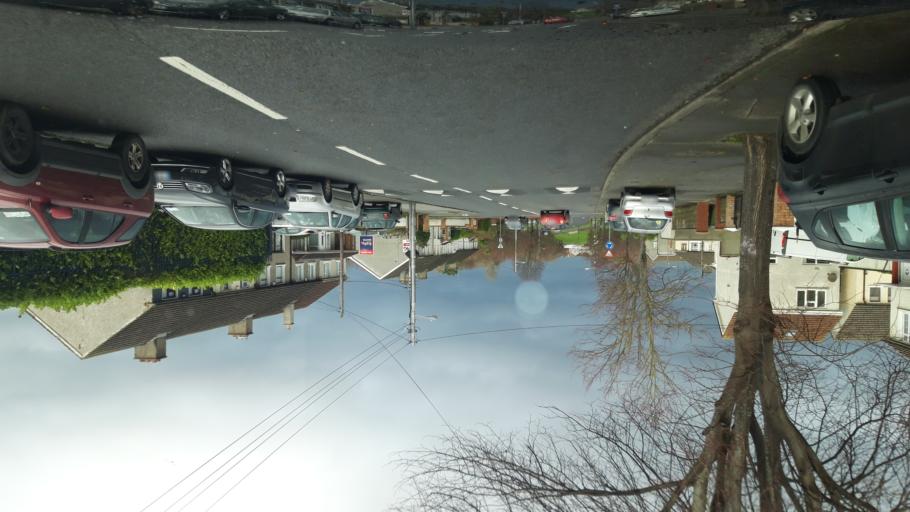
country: IE
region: Leinster
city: Raheny
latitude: 53.3808
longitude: -6.1870
